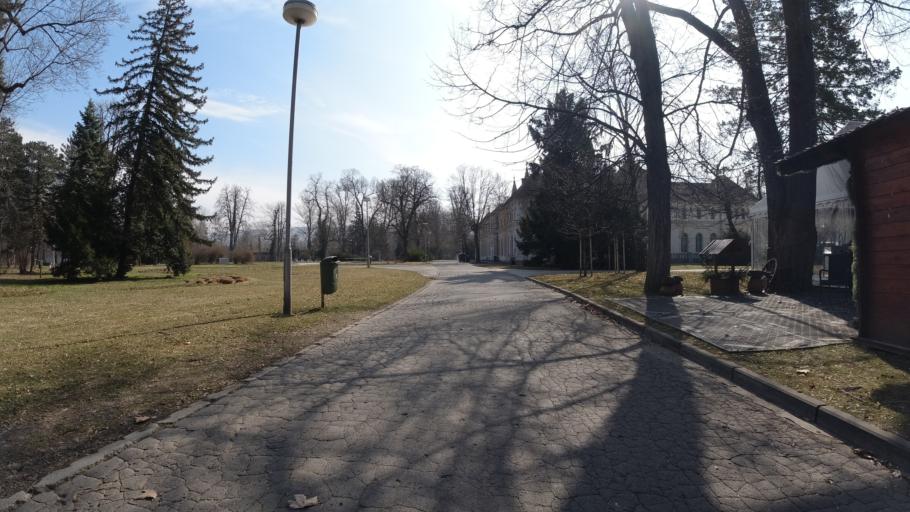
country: SK
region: Trnavsky
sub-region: Okres Trnava
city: Piestany
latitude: 48.5912
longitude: 17.8372
